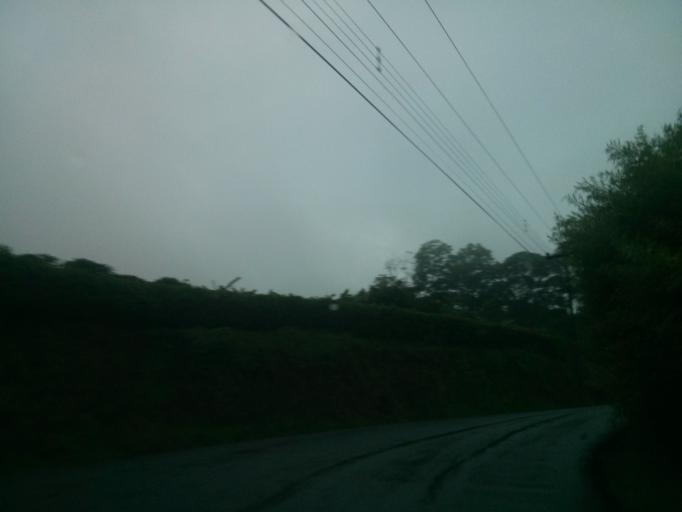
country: CR
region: Alajuela
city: Sabanilla
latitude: 10.0959
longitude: -84.1886
